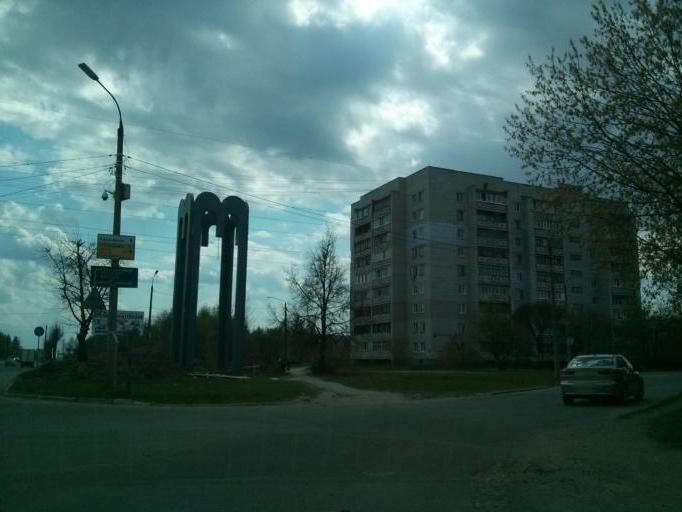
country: RU
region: Vladimir
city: Murom
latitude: 55.5534
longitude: 42.0620
